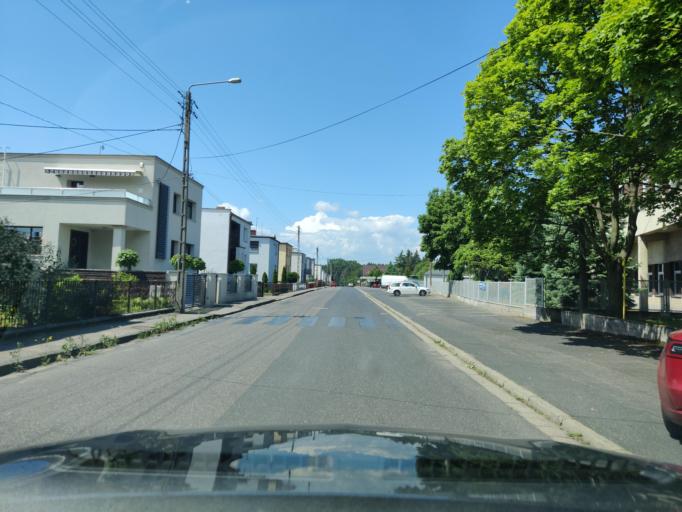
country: PL
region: Greater Poland Voivodeship
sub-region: Powiat wolsztynski
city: Wolsztyn
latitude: 52.1296
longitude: 16.1302
